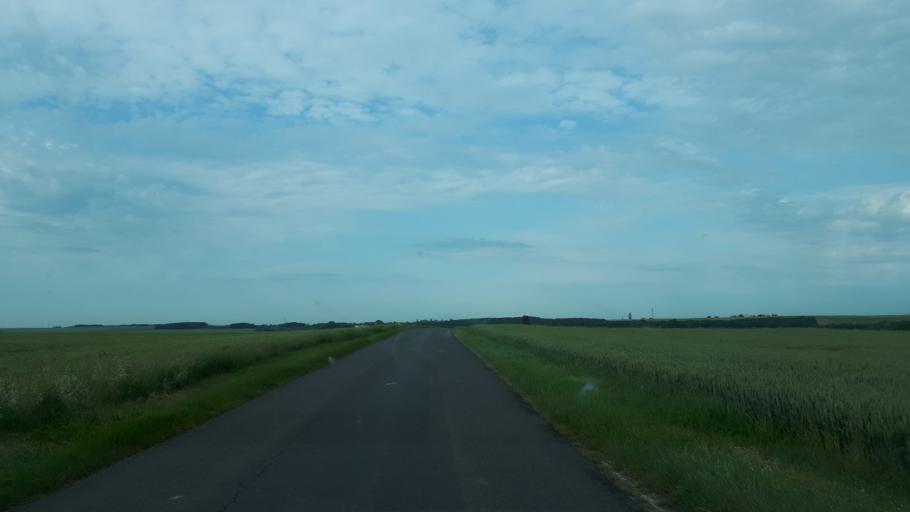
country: FR
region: Centre
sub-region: Departement du Loir-et-Cher
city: Naveil
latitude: 47.7674
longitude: 1.0107
